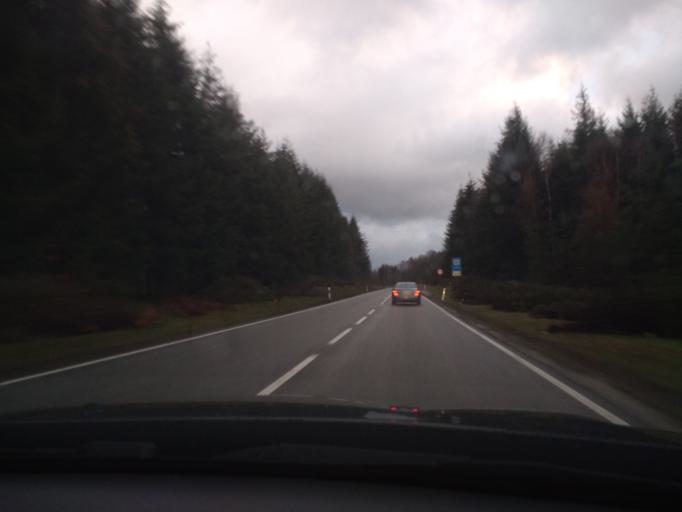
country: DE
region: Rheinland-Pfalz
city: Talling
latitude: 49.7640
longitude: 6.9619
